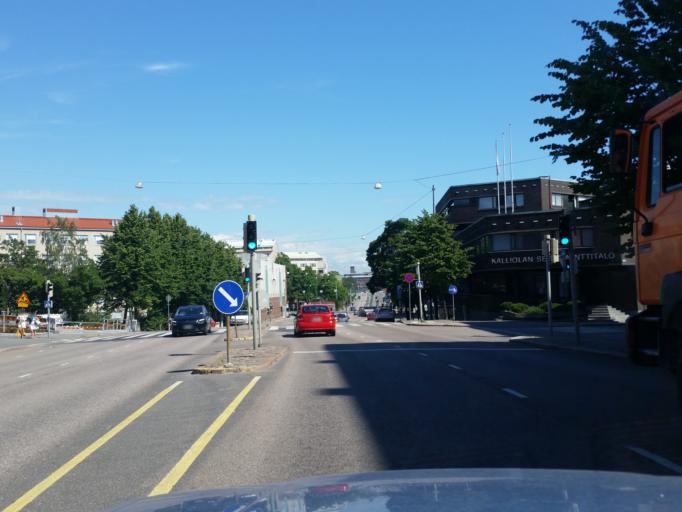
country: FI
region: Uusimaa
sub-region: Helsinki
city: Helsinki
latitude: 60.1880
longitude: 24.9449
